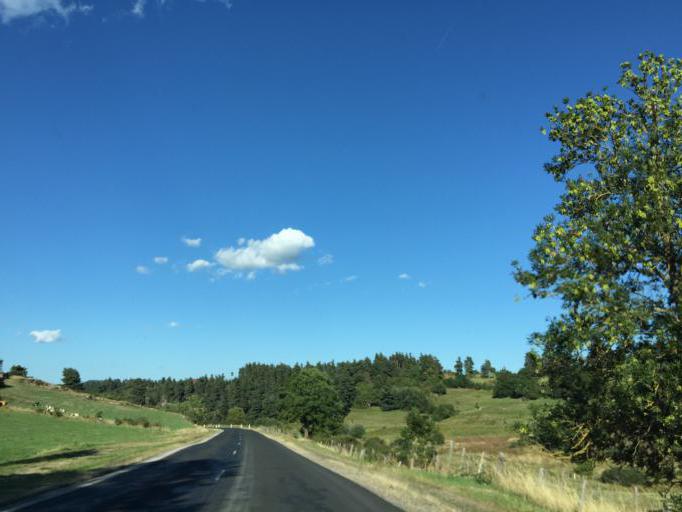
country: FR
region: Auvergne
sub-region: Departement de la Haute-Loire
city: Saugues
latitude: 44.9642
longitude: 3.6054
